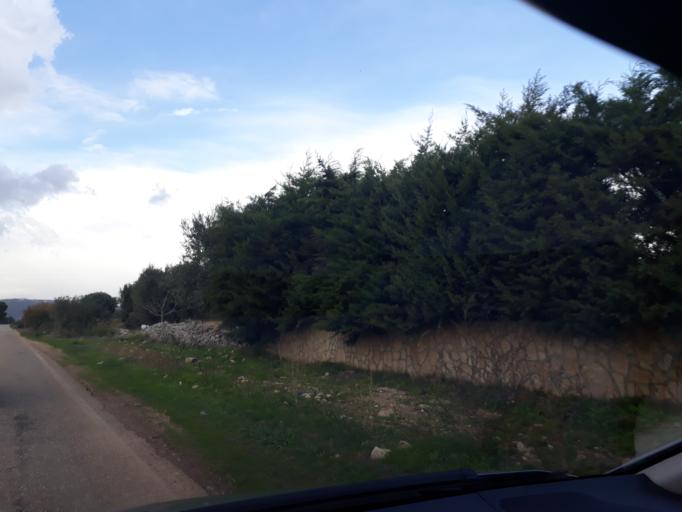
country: IT
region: Apulia
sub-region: Provincia di Brindisi
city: Pezze di Greco
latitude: 40.8020
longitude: 17.3988
